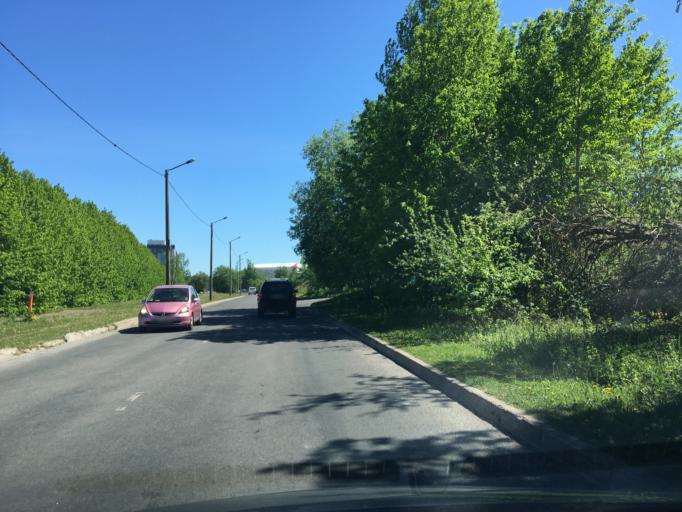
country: EE
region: Harju
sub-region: Saue vald
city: Laagri
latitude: 59.3972
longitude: 24.6515
